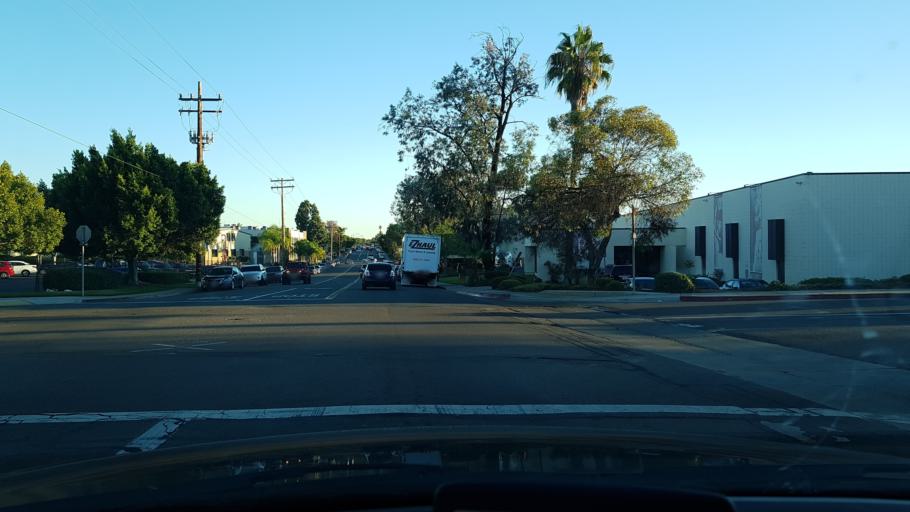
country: US
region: California
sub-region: San Diego County
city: San Diego
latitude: 32.8274
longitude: -117.1582
